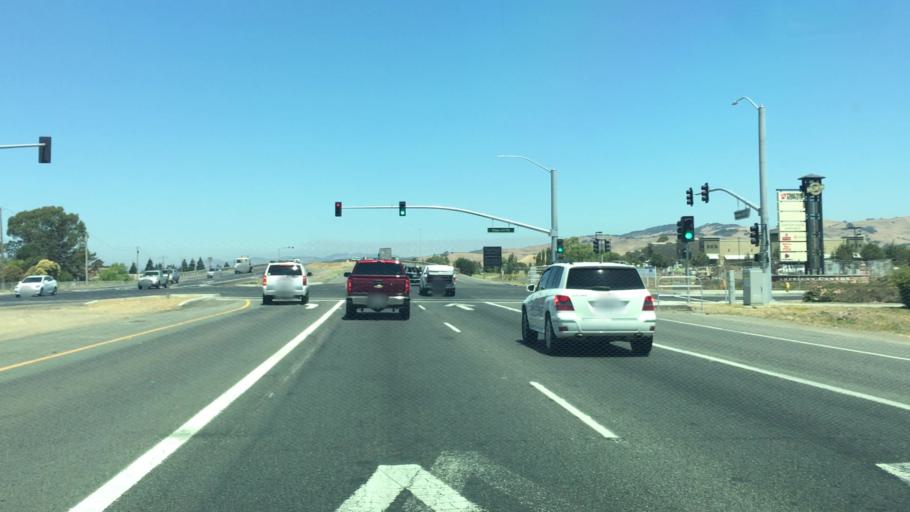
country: US
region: California
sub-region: Napa County
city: American Canyon
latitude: 38.1844
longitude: -122.2552
